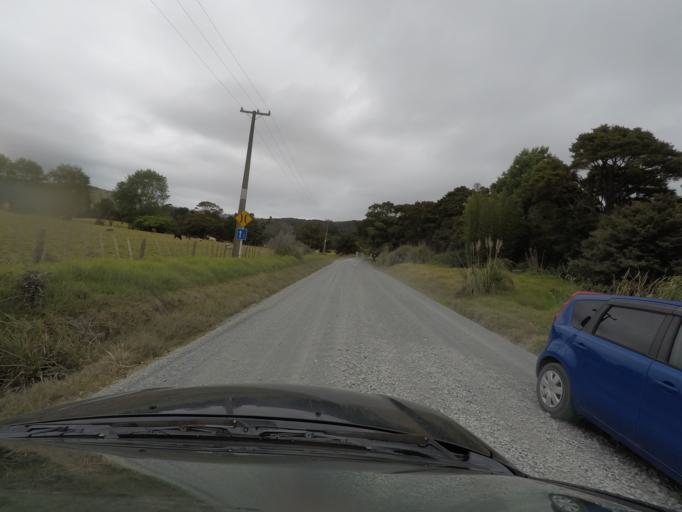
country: NZ
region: Auckland
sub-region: Auckland
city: Warkworth
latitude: -36.2612
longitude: 174.7258
